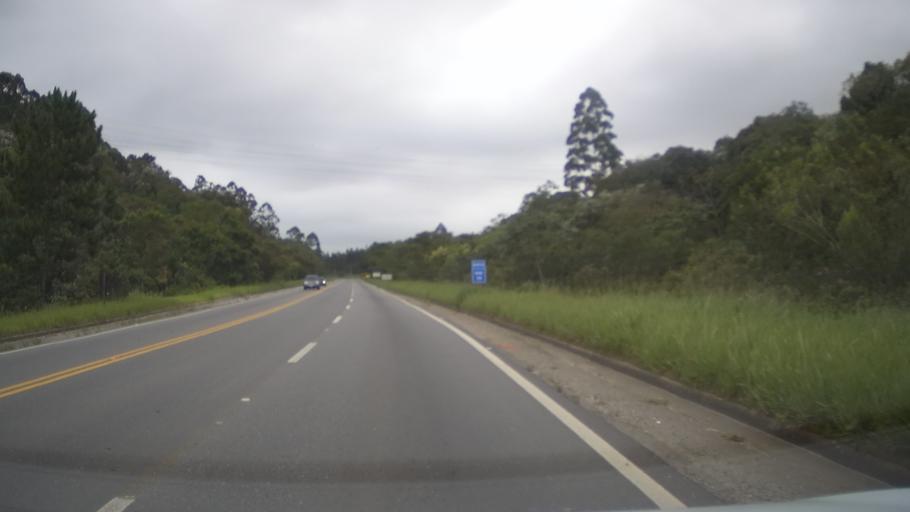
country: BR
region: Sao Paulo
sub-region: Aruja
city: Aruja
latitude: -23.3685
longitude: -46.4252
